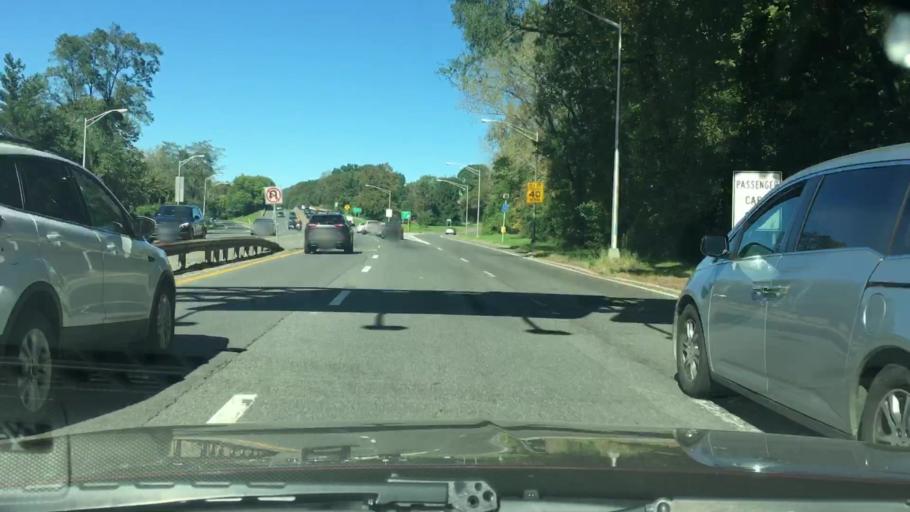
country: US
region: New York
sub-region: Westchester County
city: Pelham Manor
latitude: 40.8888
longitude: -73.8152
